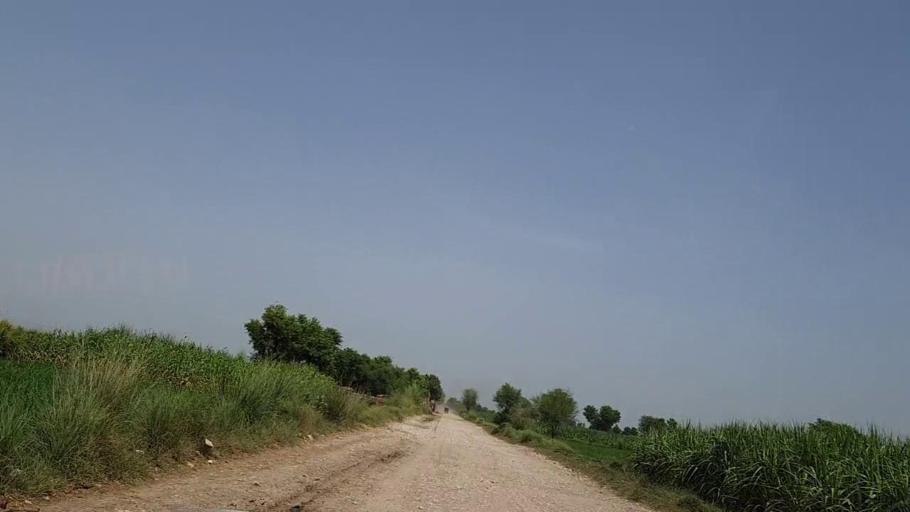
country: PK
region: Sindh
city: Tharu Shah
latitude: 26.9002
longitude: 68.0078
